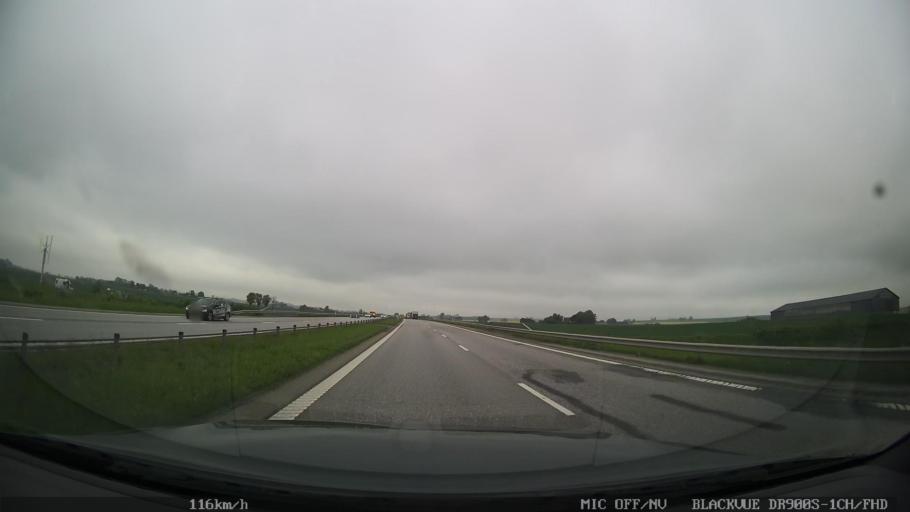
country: SE
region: Skane
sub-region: Landskrona
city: Landskrona
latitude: 55.8981
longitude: 12.8673
